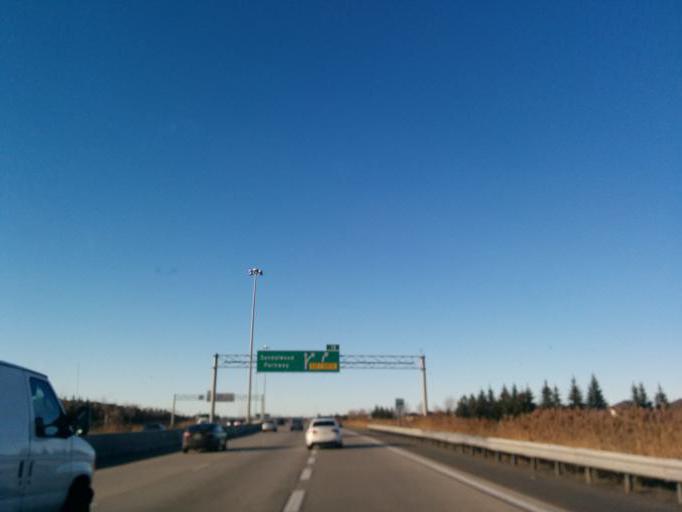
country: CA
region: Ontario
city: Brampton
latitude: 43.7316
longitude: -79.7699
